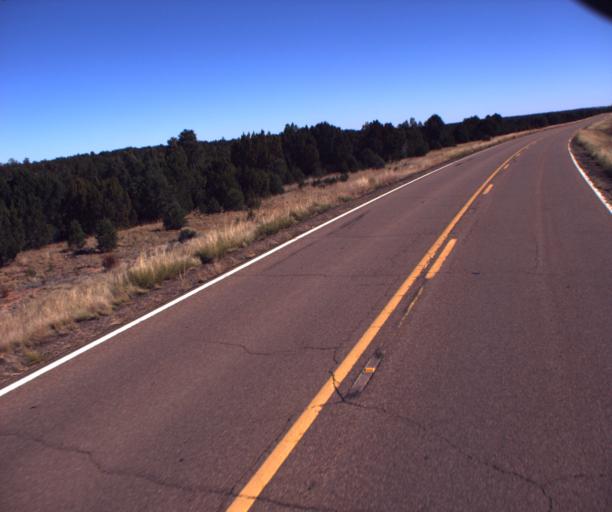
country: US
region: Arizona
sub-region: Navajo County
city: Heber-Overgaard
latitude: 34.4560
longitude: -110.5200
